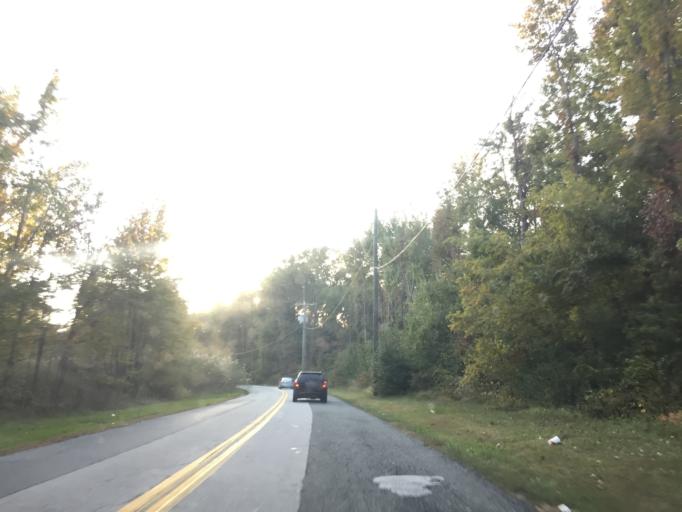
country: US
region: Maryland
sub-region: Baltimore County
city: Essex
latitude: 39.2971
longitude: -76.4440
